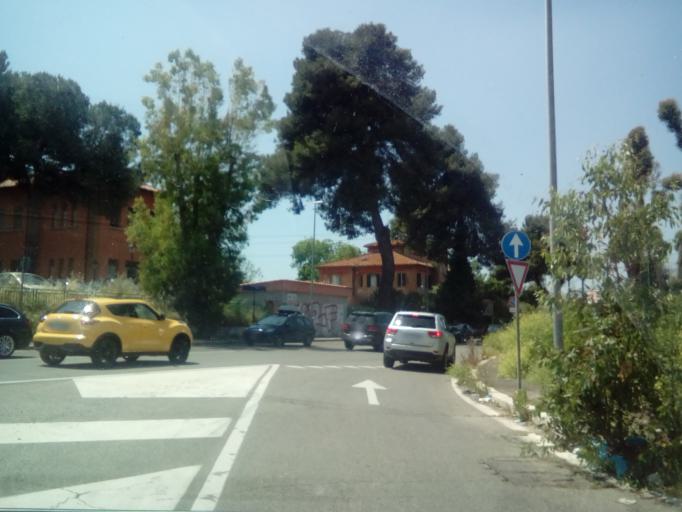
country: IT
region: Latium
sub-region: Citta metropolitana di Roma Capitale
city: Selcetta
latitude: 41.8015
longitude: 12.4806
